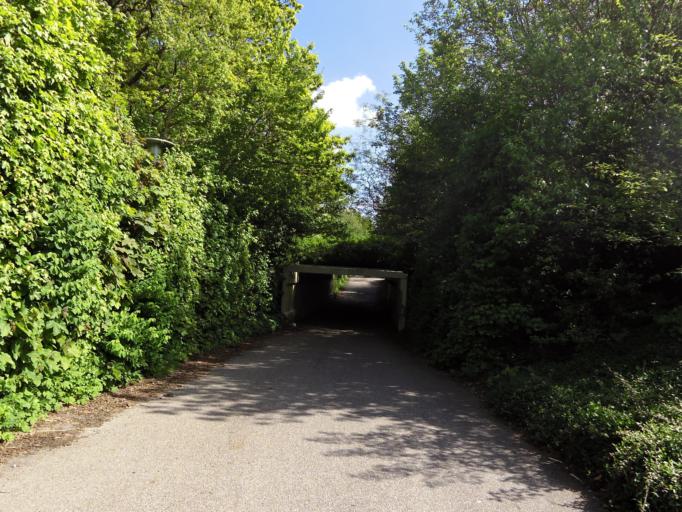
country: DK
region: South Denmark
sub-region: Tonder Kommune
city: Toftlund
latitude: 55.1881
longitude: 9.0690
